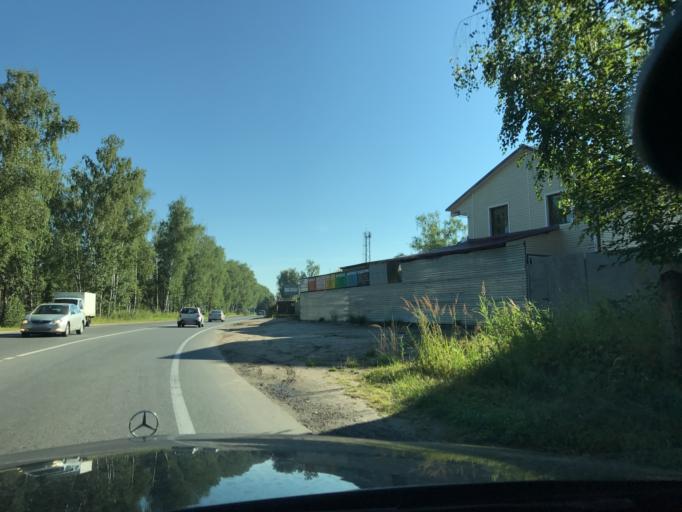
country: RU
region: Moskovskaya
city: Chernogolovka
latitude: 55.9943
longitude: 38.3534
